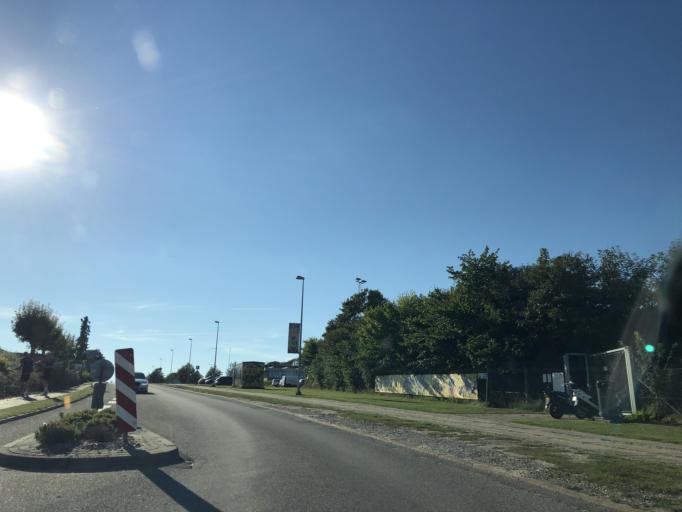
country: DK
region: North Denmark
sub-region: Mariagerfjord Kommune
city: Hobro
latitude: 56.6337
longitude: 9.8179
